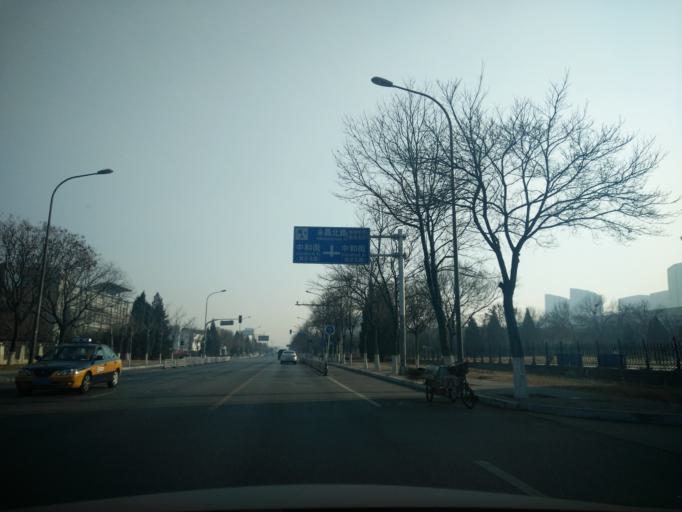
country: CN
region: Beijing
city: Jiugong
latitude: 39.7990
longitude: 116.5076
